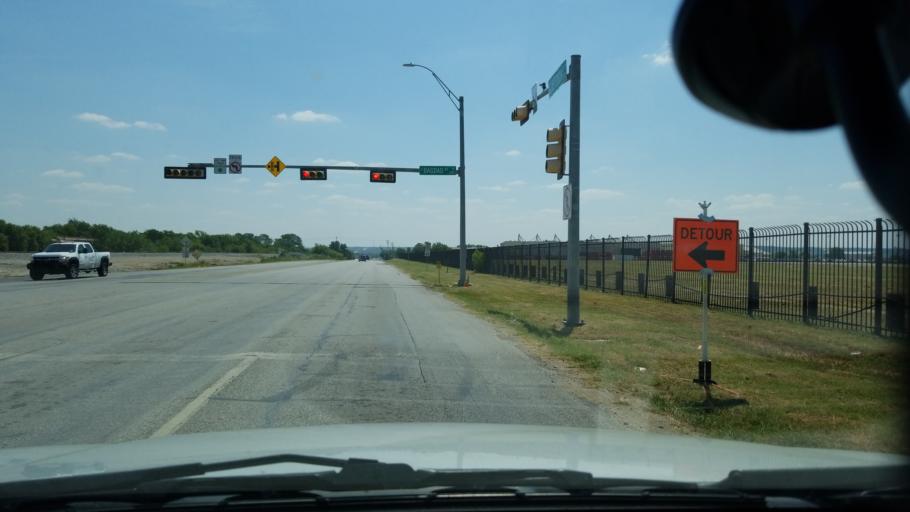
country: US
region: Texas
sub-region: Dallas County
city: Grand Prairie
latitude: 32.7458
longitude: -96.9710
